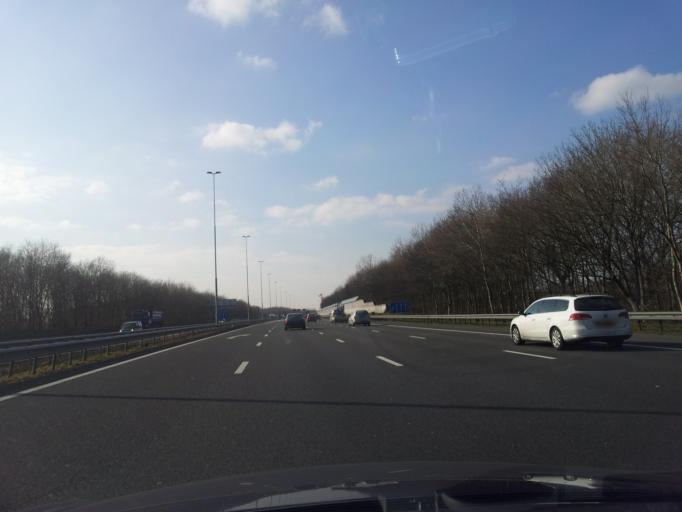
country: NL
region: North Holland
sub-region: Gemeente Ouder-Amstel
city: Ouderkerk aan de Amstel
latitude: 52.2871
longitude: 4.9239
